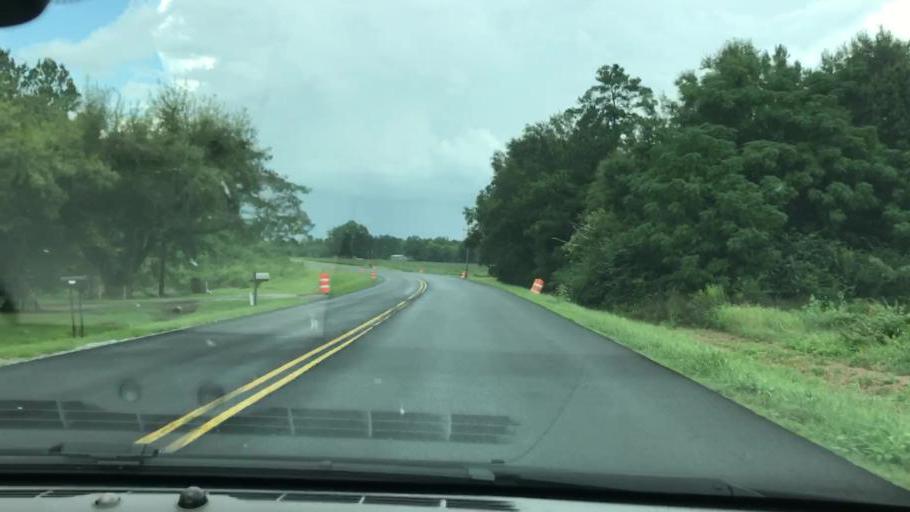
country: US
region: Georgia
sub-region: Early County
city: Blakely
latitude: 31.4186
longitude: -84.9630
